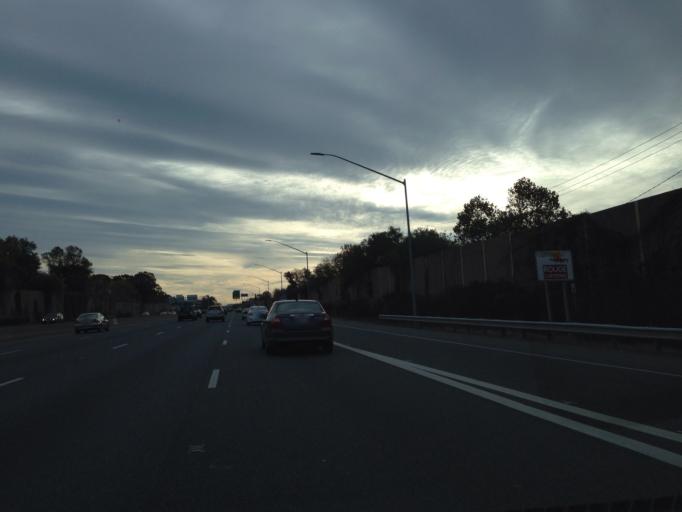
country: US
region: Maryland
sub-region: Baltimore County
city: Lutherville
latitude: 39.4155
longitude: -76.6262
